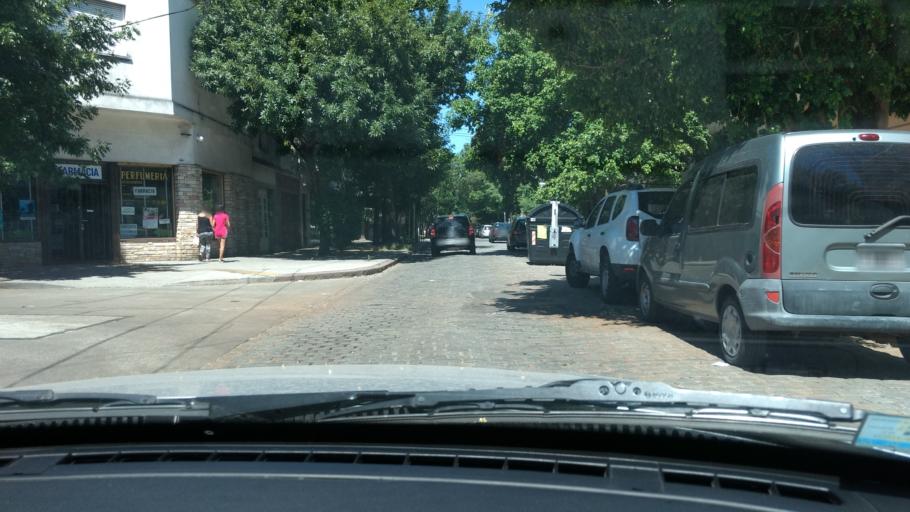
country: AR
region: Buenos Aires F.D.
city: Villa Santa Rita
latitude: -34.6286
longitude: -58.5252
